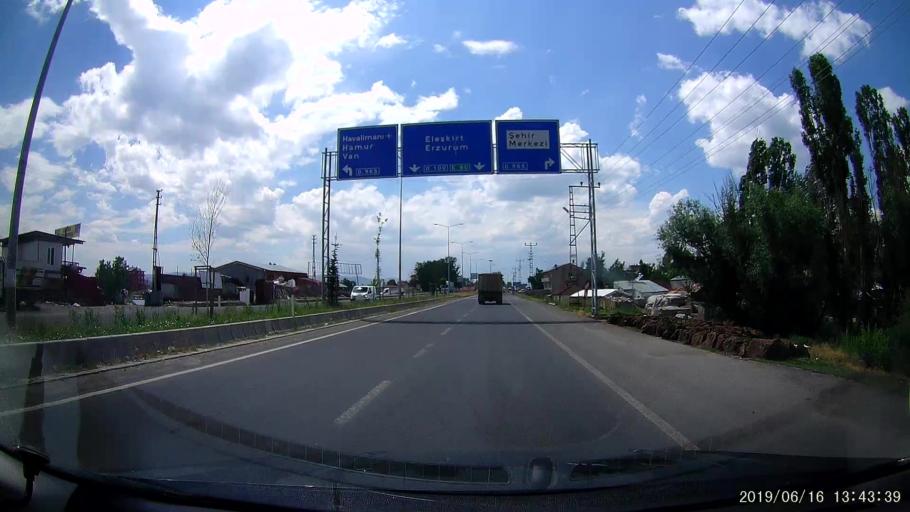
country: TR
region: Agri
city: Agri
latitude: 39.7080
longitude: 43.0520
